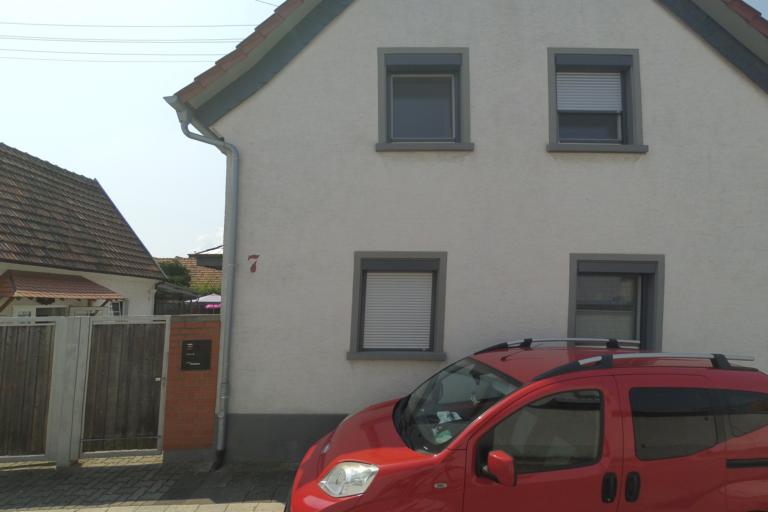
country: DE
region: Rheinland-Pfalz
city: Gartenstadt
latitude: 49.4560
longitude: 8.3789
